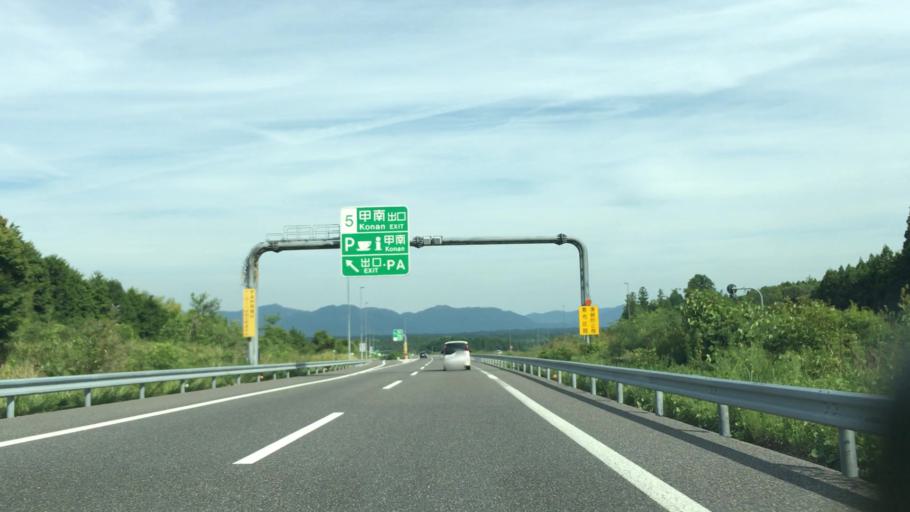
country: JP
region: Shiga Prefecture
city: Minakuchicho-matoba
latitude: 34.9175
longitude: 136.1459
